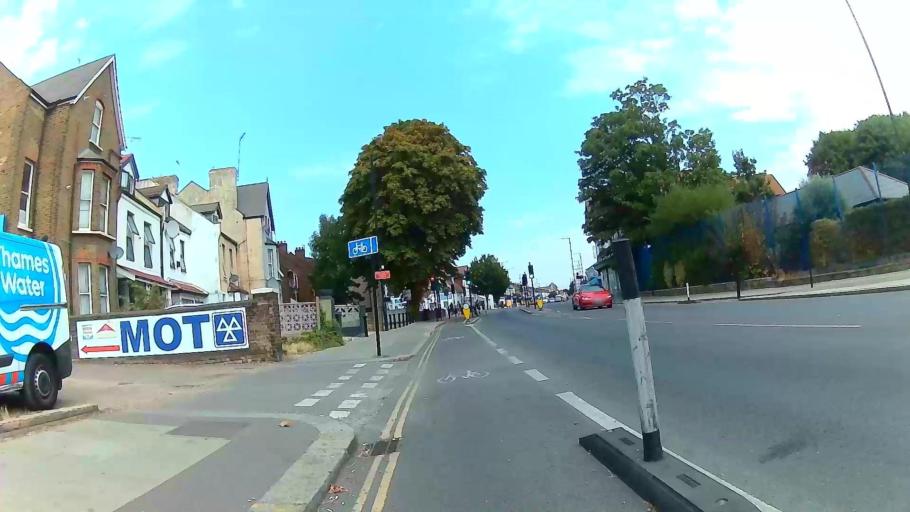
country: GB
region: England
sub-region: Greater London
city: Enfield
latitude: 51.6296
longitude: -0.0563
